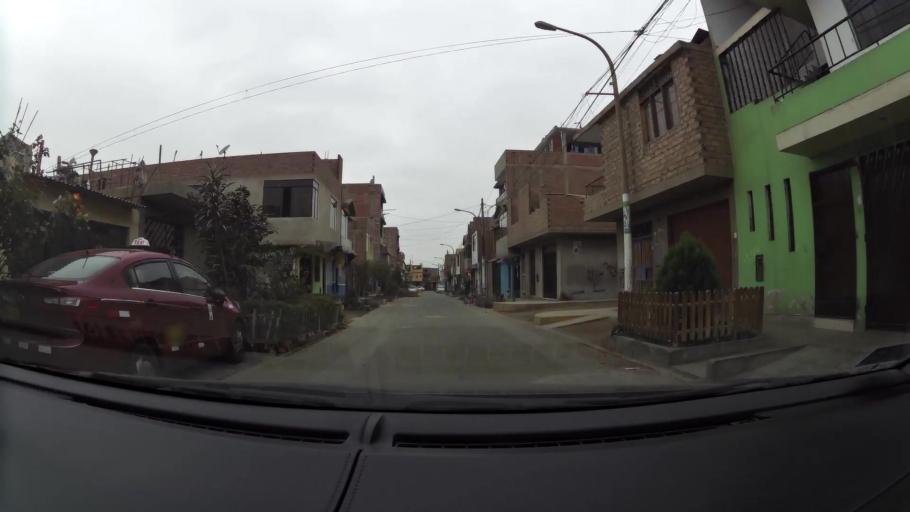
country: PE
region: Lima
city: Ventanilla
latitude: -11.9325
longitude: -77.0844
